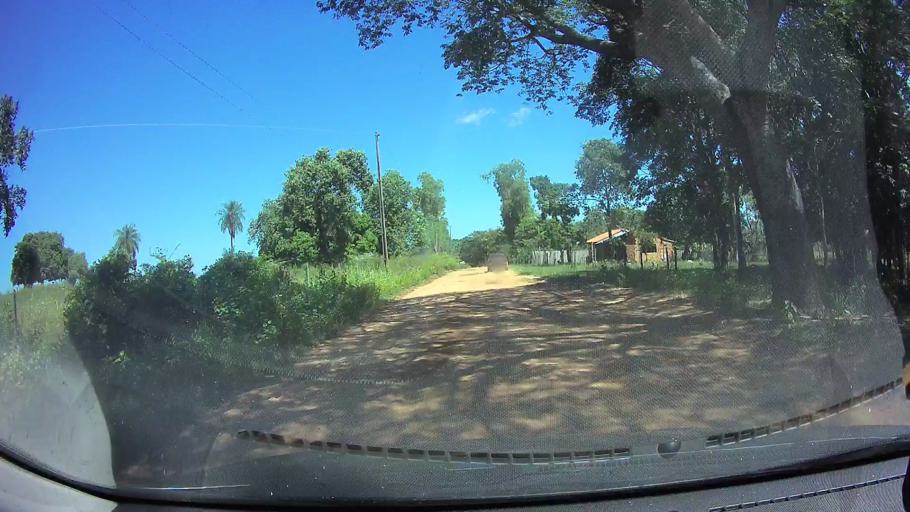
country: PY
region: Cordillera
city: Arroyos y Esteros
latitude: -24.9827
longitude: -57.2122
